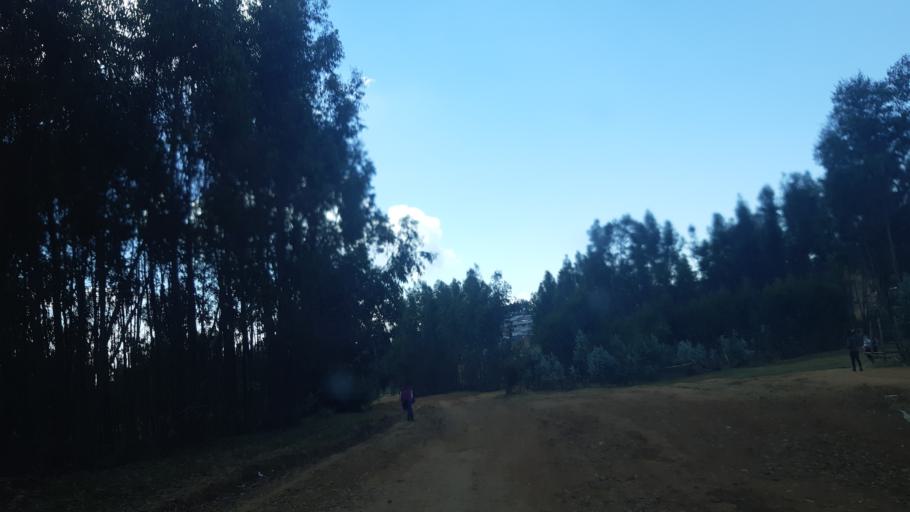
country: ET
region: Amhara
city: Dabat
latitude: 13.3590
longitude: 37.3846
